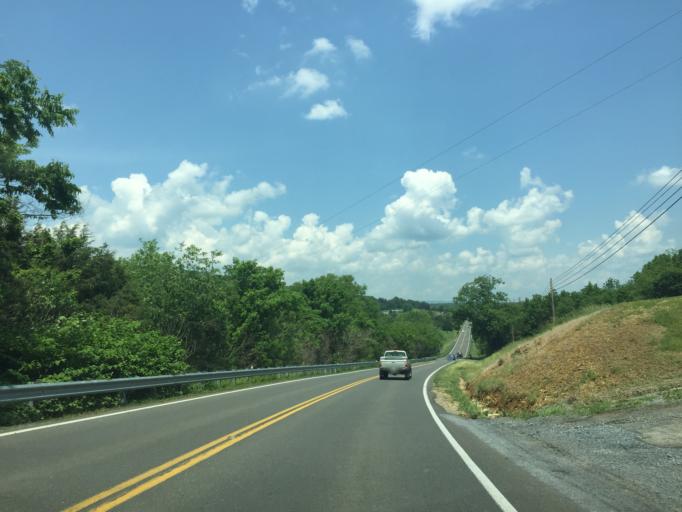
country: US
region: Virginia
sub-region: Shenandoah County
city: Strasburg
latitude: 39.0617
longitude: -78.3725
